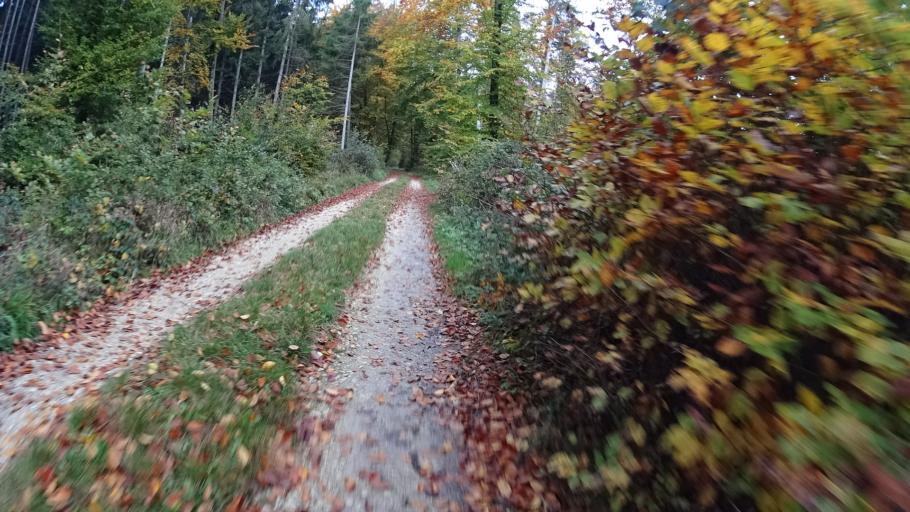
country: DE
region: Bavaria
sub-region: Upper Bavaria
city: Adelschlag
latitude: 48.8726
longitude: 11.2587
